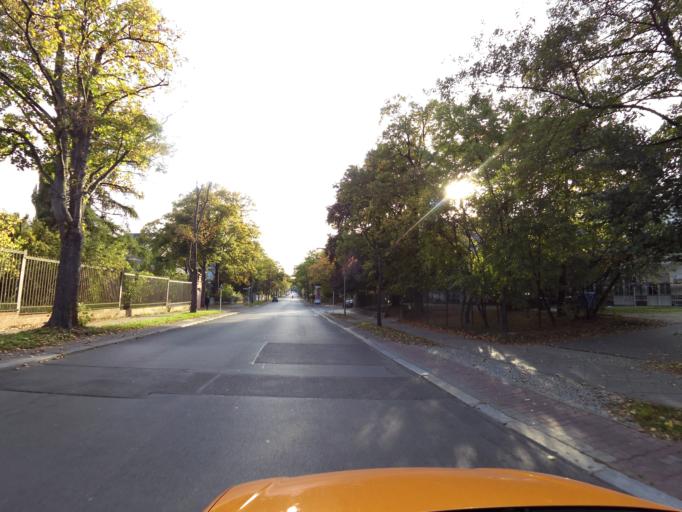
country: DE
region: Berlin
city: Dahlem
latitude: 52.4550
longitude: 13.2999
